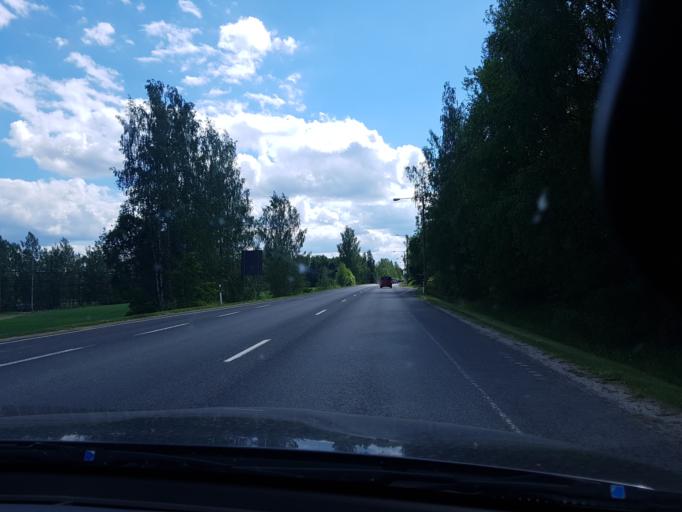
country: FI
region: Haeme
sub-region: Haemeenlinna
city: Parola
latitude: 61.0683
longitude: 24.3922
